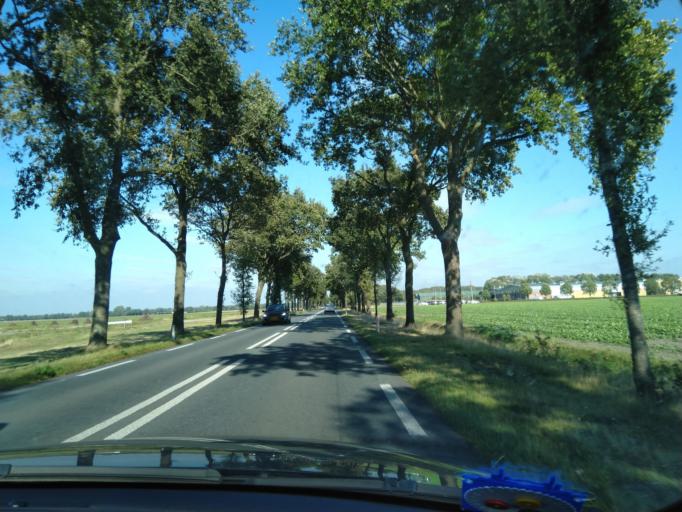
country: NL
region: Groningen
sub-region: Gemeente Pekela
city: Oude Pekela
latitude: 53.0928
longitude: 6.9757
